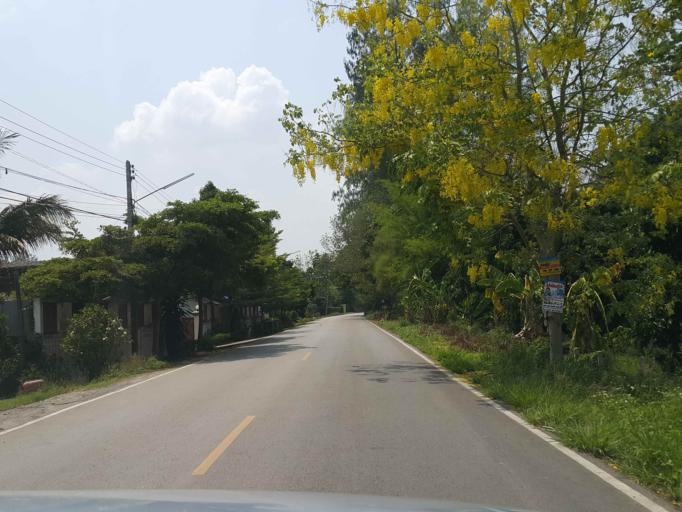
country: TH
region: Chiang Mai
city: Saraphi
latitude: 18.6816
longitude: 99.0022
